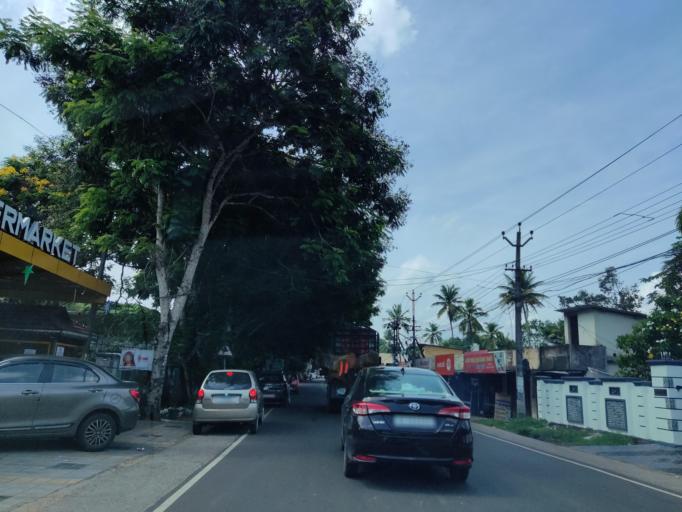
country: IN
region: Kerala
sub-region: Alappuzha
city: Mavelikara
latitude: 9.2876
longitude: 76.5320
